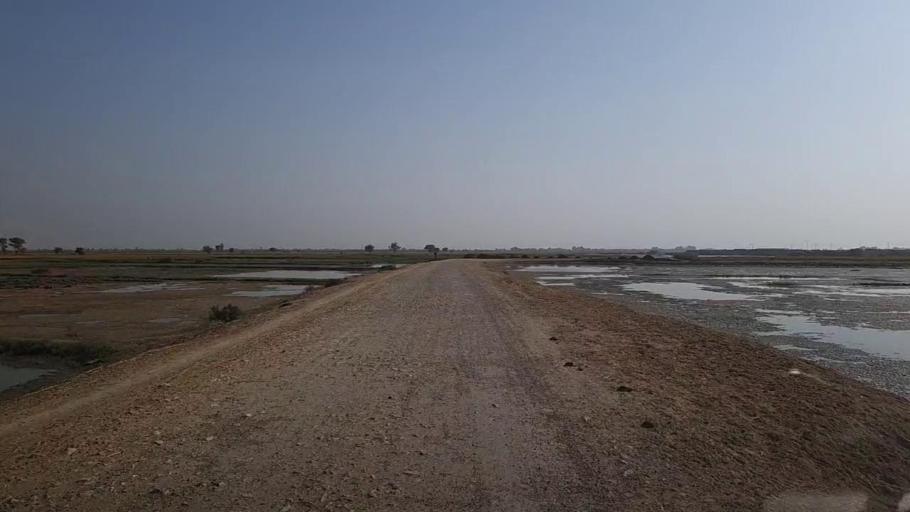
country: PK
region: Sindh
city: Kandhkot
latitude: 28.3739
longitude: 69.3331
